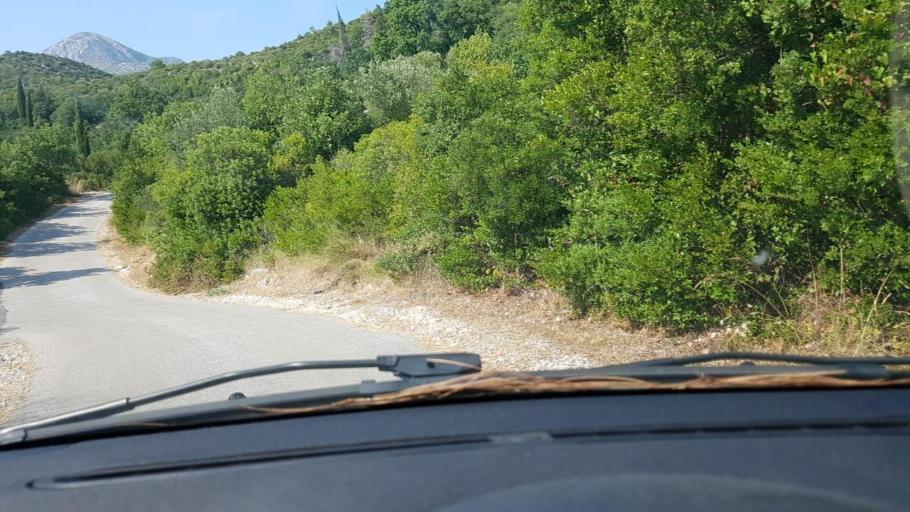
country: HR
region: Dubrovacko-Neretvanska
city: Podgora
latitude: 42.7818
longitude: 17.8623
